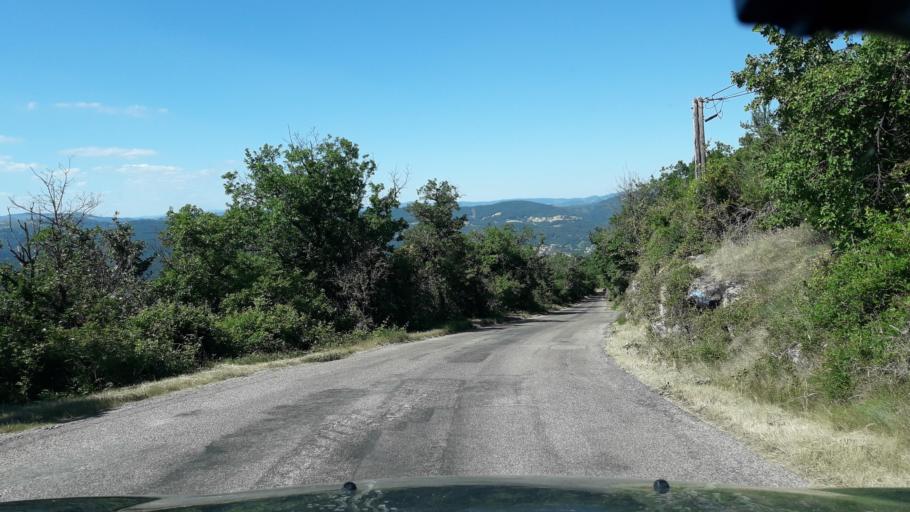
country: FR
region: Rhone-Alpes
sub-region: Departement de l'Ardeche
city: Privas
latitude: 44.7006
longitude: 4.5830
